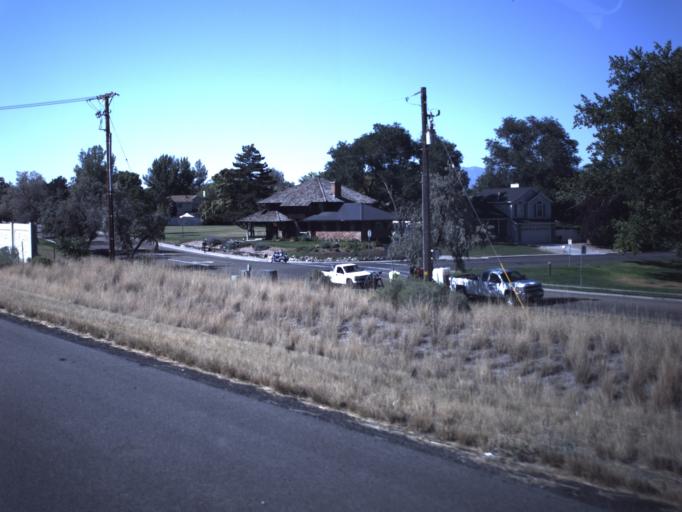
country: US
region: Utah
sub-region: Tooele County
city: Stansbury park
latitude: 40.6428
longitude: -112.2879
